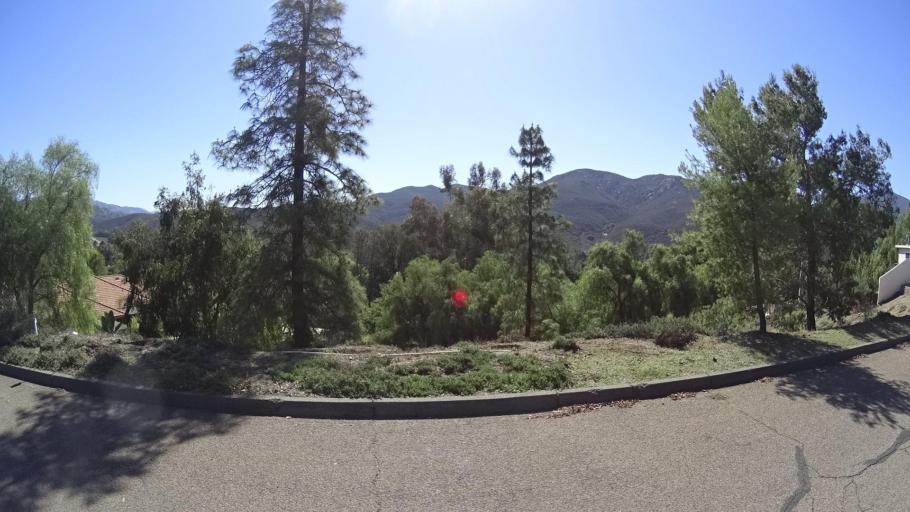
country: US
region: California
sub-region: San Diego County
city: Rancho San Diego
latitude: 32.7297
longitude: -116.9117
